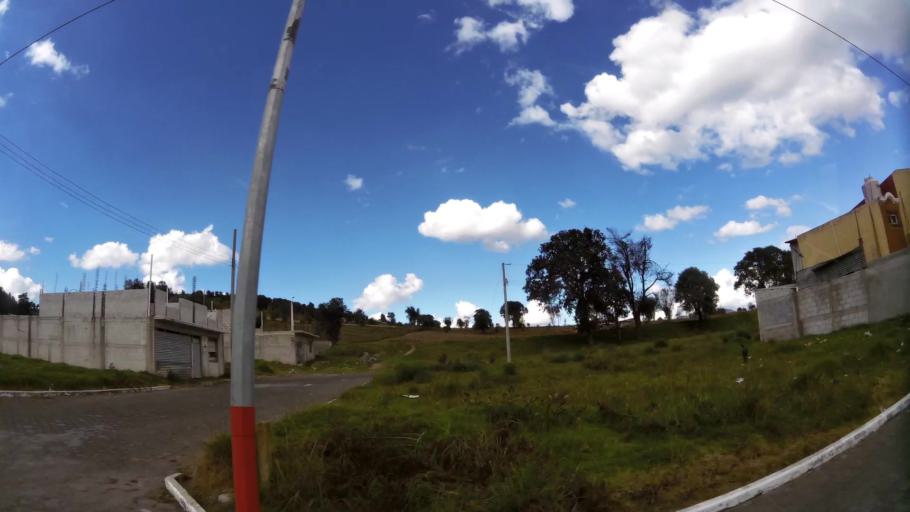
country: GT
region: Quetzaltenango
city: Quetzaltenango
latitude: 14.8359
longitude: -91.5504
